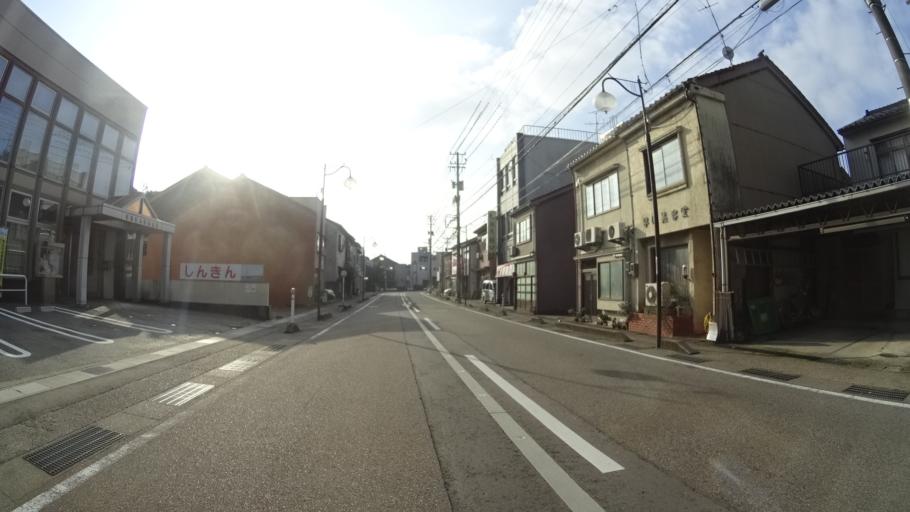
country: JP
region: Toyama
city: Himi
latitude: 36.8629
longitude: 136.9855
